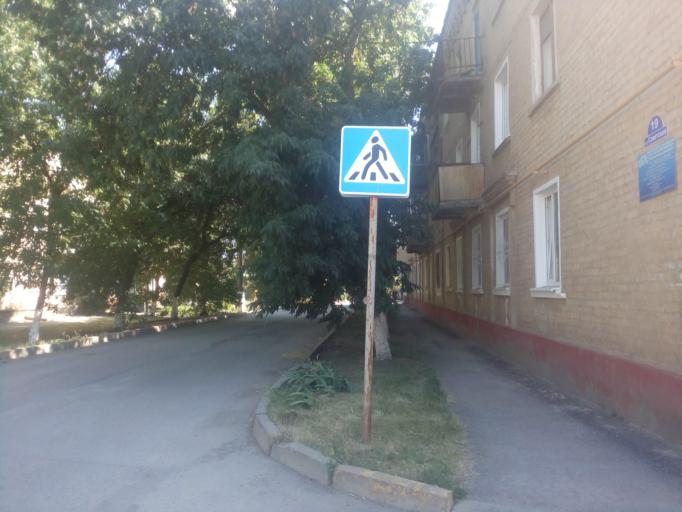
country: RU
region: Rostov
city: Sholokhovskiy
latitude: 48.2827
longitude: 41.0503
